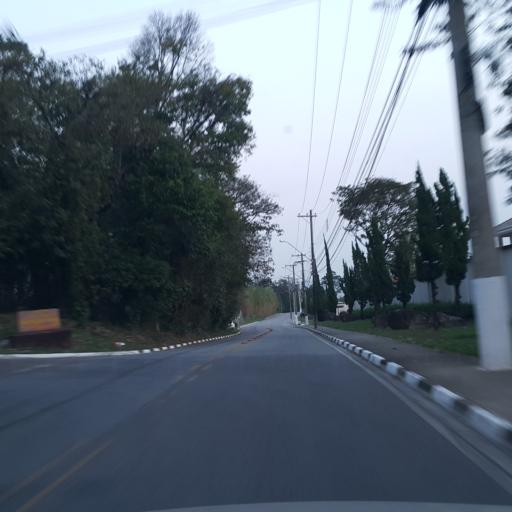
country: BR
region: Sao Paulo
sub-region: Vinhedo
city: Vinhedo
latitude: -23.0599
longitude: -46.9706
